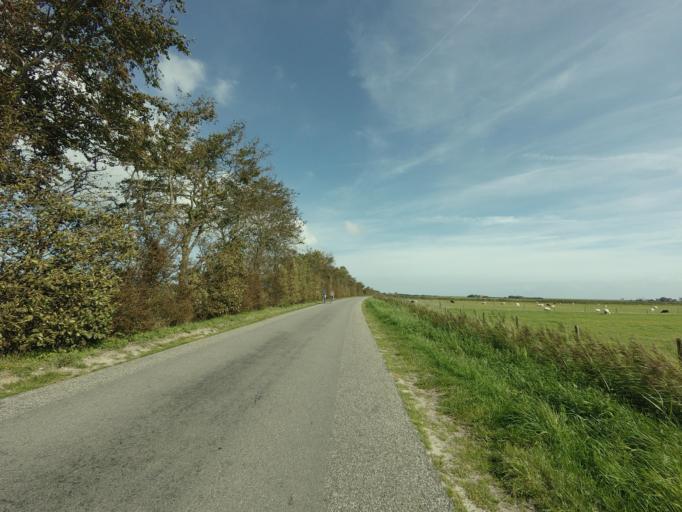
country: NL
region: Friesland
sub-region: Gemeente Ameland
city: Hollum
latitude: 53.4418
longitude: 5.6911
